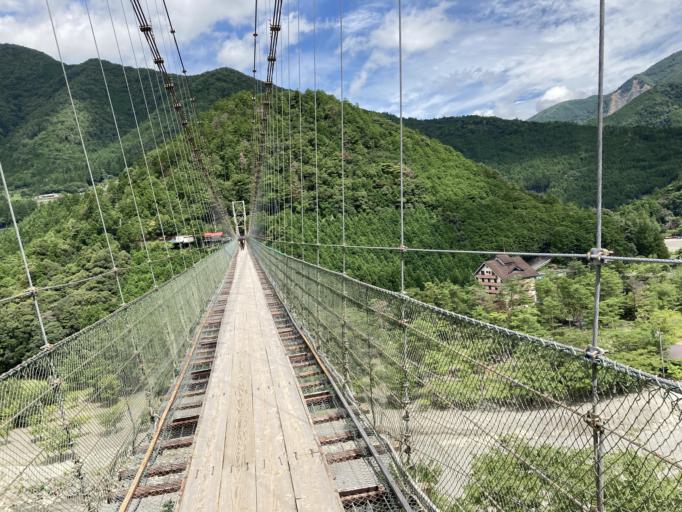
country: JP
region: Wakayama
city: Koya
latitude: 34.1007
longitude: 135.7631
